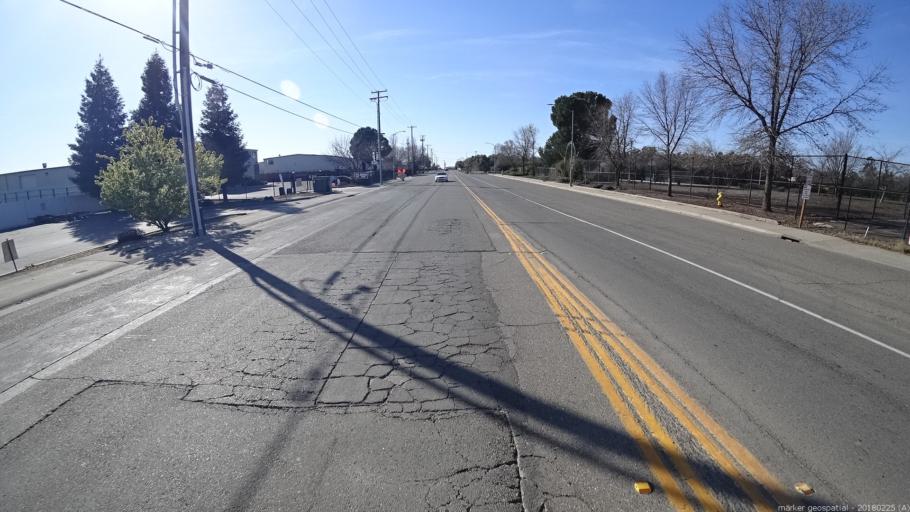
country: US
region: California
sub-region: Sacramento County
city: Antelope
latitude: 38.7190
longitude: -121.3275
